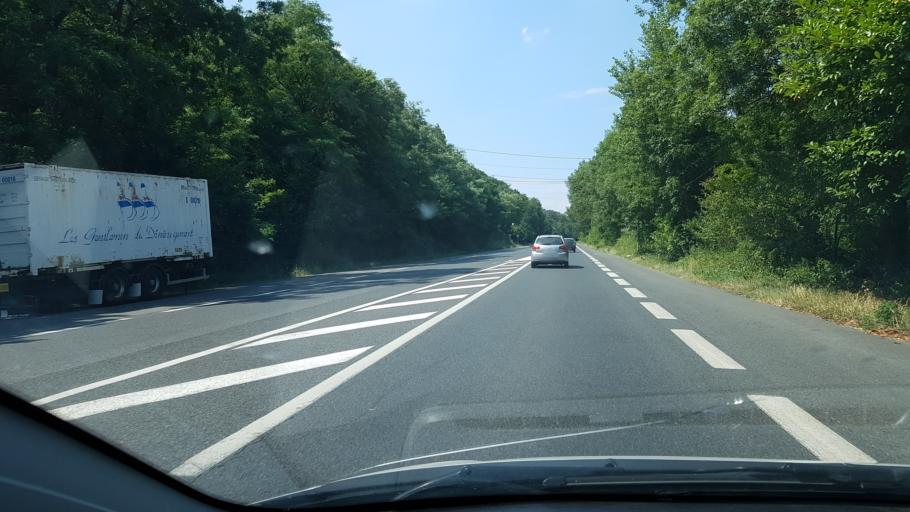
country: FR
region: Rhone-Alpes
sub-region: Departement du Rhone
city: Montagny
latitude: 45.6257
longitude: 4.7614
